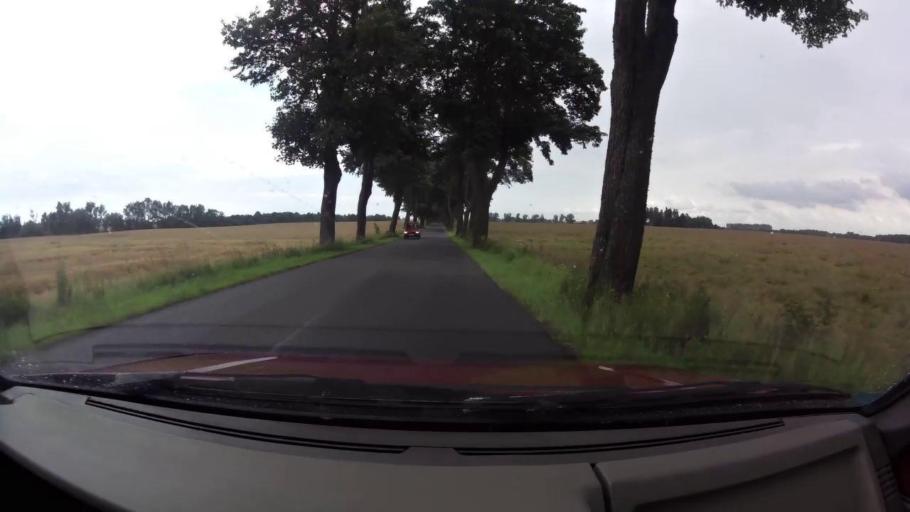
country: PL
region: West Pomeranian Voivodeship
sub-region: Koszalin
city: Koszalin
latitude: 54.1442
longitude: 16.1226
